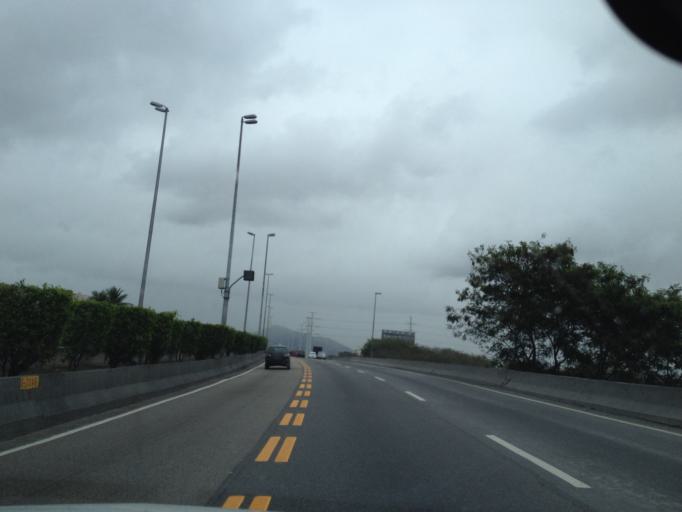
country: BR
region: Rio de Janeiro
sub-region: Rio De Janeiro
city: Rio de Janeiro
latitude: -22.8719
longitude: -43.2655
